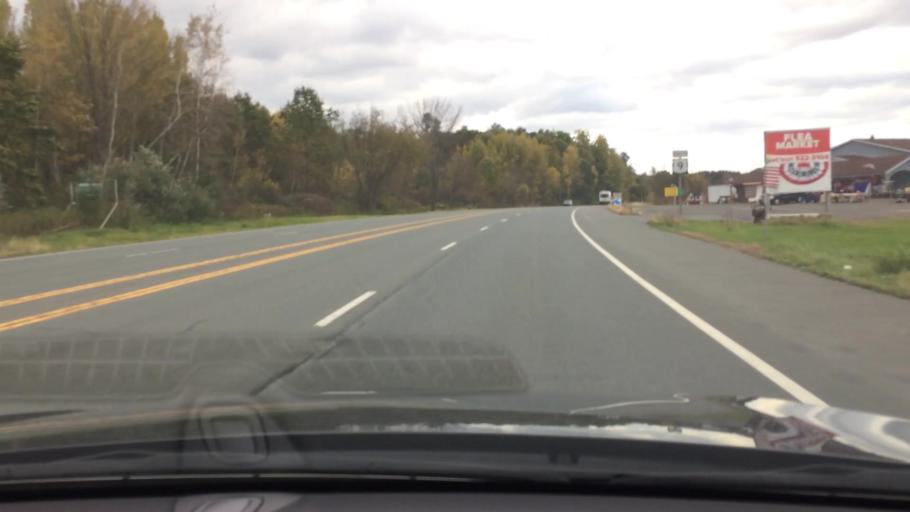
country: US
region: New York
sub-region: Columbia County
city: Niverville
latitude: 42.4791
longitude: -73.6803
